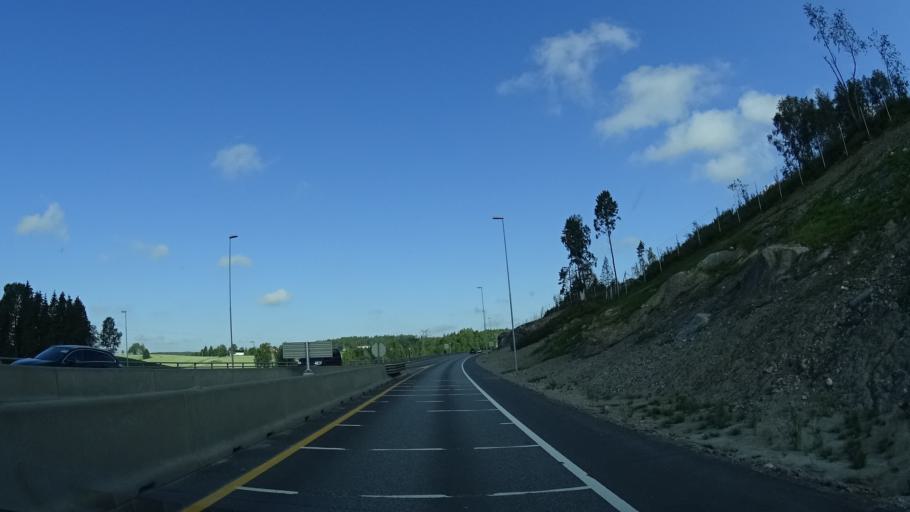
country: NO
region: Ostfold
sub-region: Hobol
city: Elvestad
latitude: 59.6445
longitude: 10.9275
